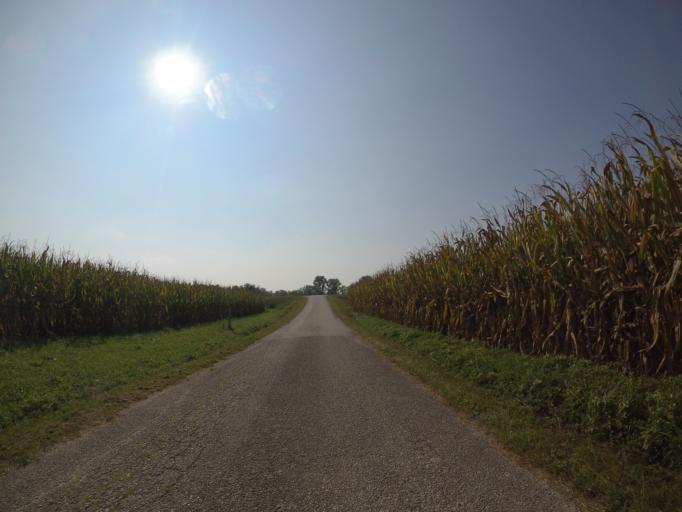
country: IT
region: Friuli Venezia Giulia
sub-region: Provincia di Udine
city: Camino al Tagliamento
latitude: 45.9098
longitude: 12.9327
